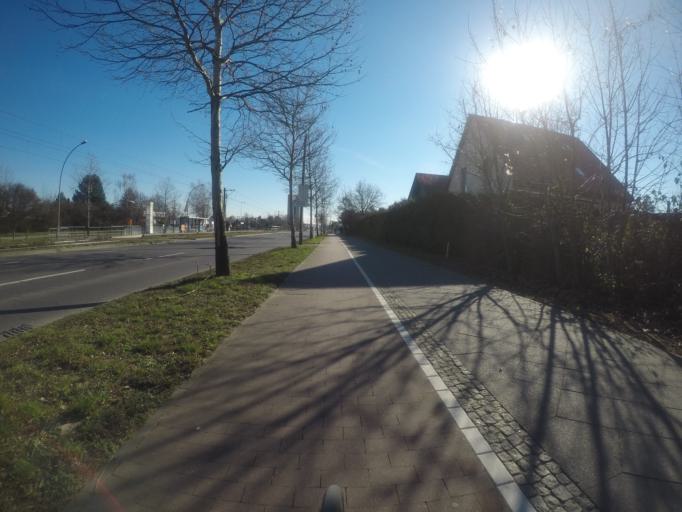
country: DE
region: Berlin
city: Alt-Hohenschoenhausen
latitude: 52.5405
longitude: 13.5133
